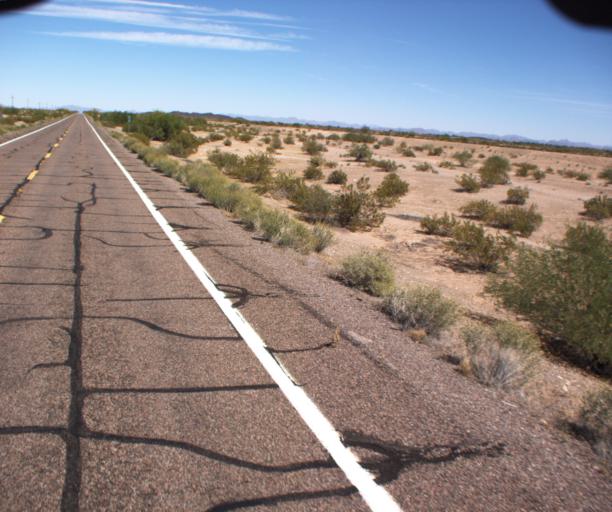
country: US
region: Arizona
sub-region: Maricopa County
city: Gila Bend
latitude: 32.7787
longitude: -112.8115
